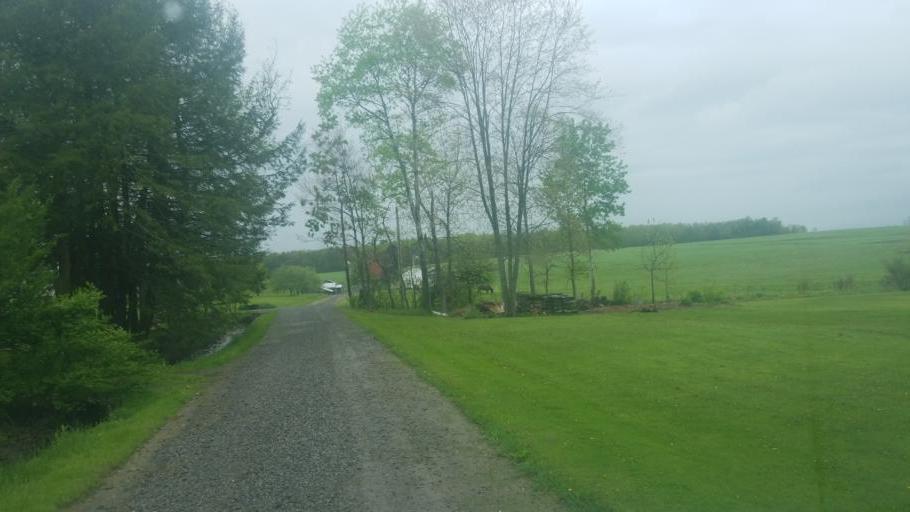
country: US
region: Pennsylvania
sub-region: Forest County
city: Tionesta
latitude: 41.3966
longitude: -79.3897
